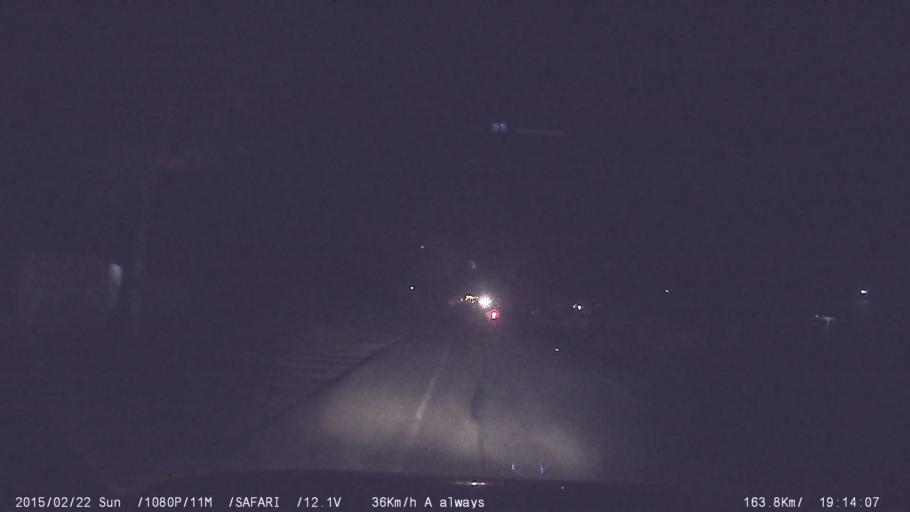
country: IN
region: Tamil Nadu
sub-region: Theni
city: Periyakulam
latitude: 10.0828
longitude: 77.5206
